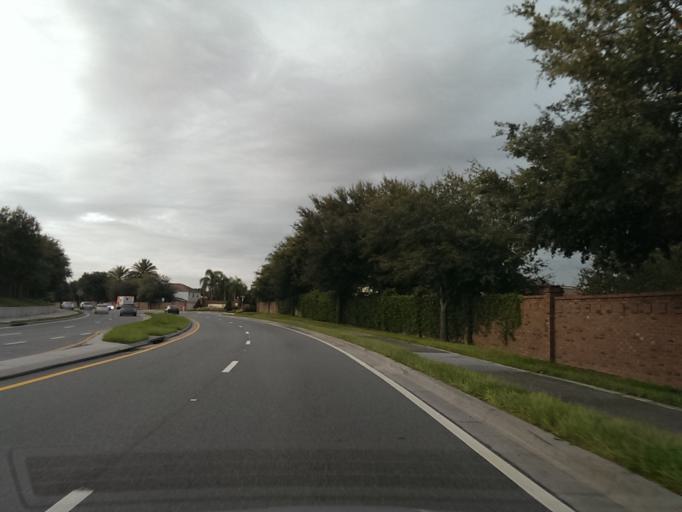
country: US
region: Florida
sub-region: Orange County
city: Lake Butler
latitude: 28.5106
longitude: -81.5841
